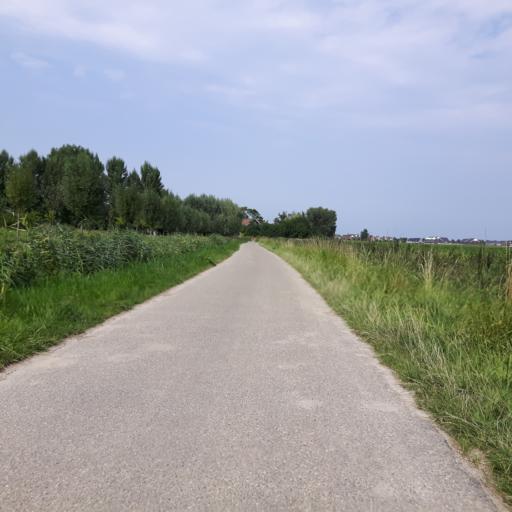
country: NL
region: Zeeland
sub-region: Gemeente Goes
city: Goes
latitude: 51.5076
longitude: 3.9107
